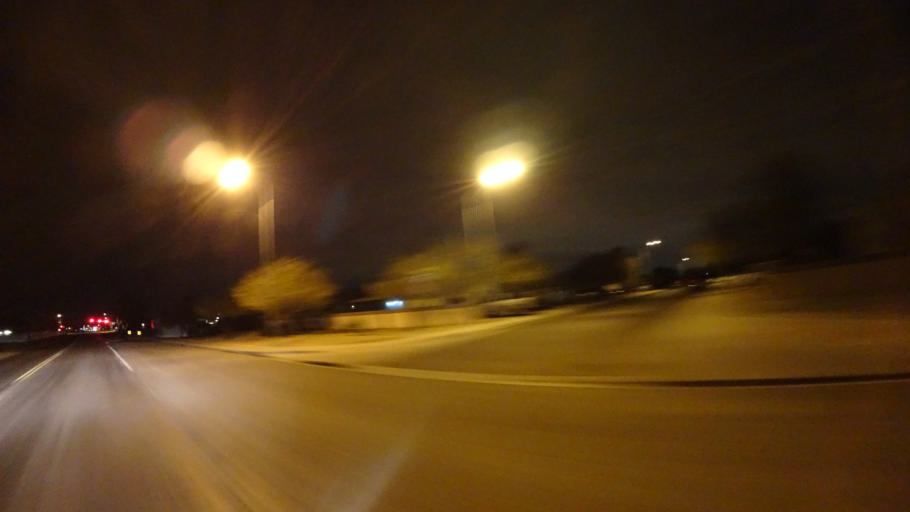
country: US
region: Arizona
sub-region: Pinal County
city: Apache Junction
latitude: 33.4247
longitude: -111.5634
